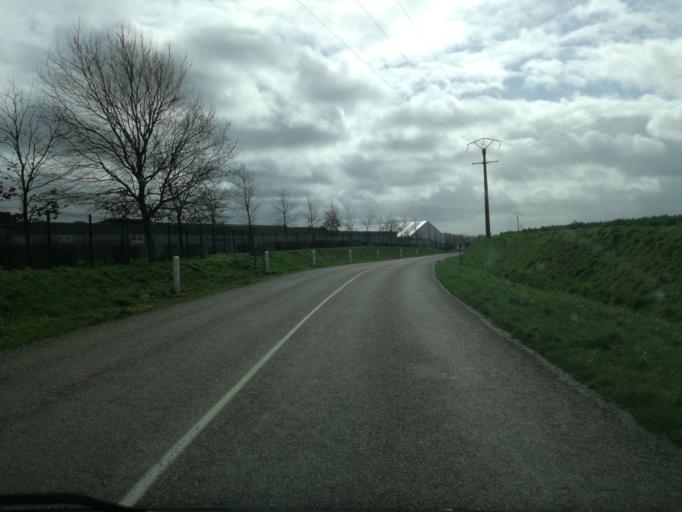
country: FR
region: Haute-Normandie
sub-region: Departement de la Seine-Maritime
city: Valliquerville
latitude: 49.6100
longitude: 0.6657
